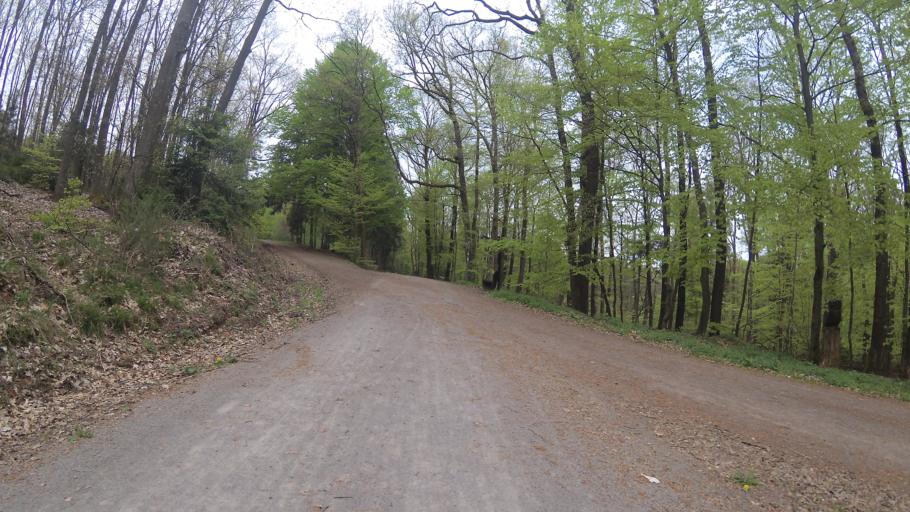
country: DE
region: Saarland
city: Mainzweiler
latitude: 49.3996
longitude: 7.1245
